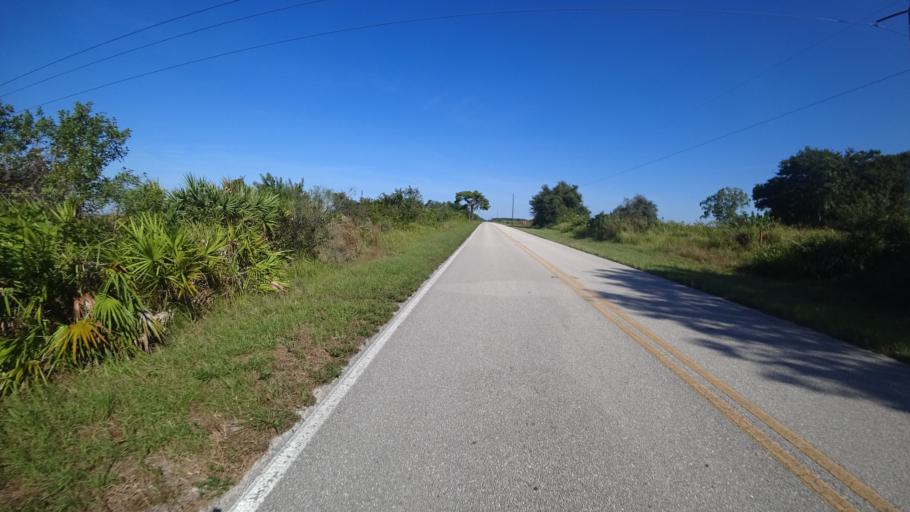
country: US
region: Florida
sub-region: Hillsborough County
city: Wimauma
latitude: 27.6031
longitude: -82.2928
